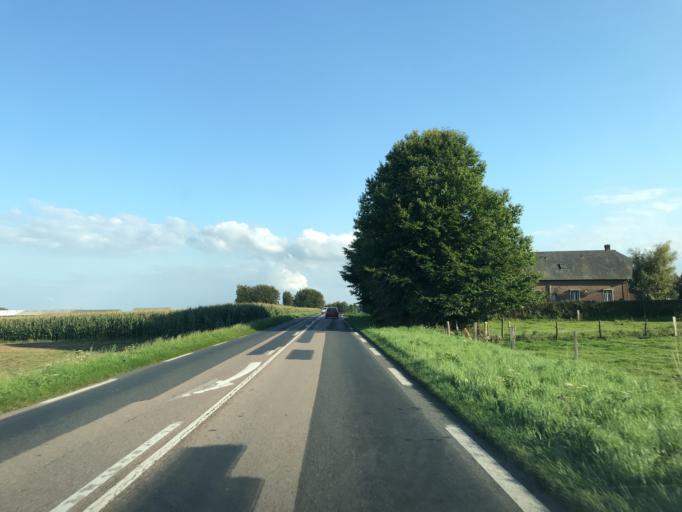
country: FR
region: Haute-Normandie
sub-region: Departement de la Seine-Maritime
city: Breaute
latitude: 49.6095
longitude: 0.4119
